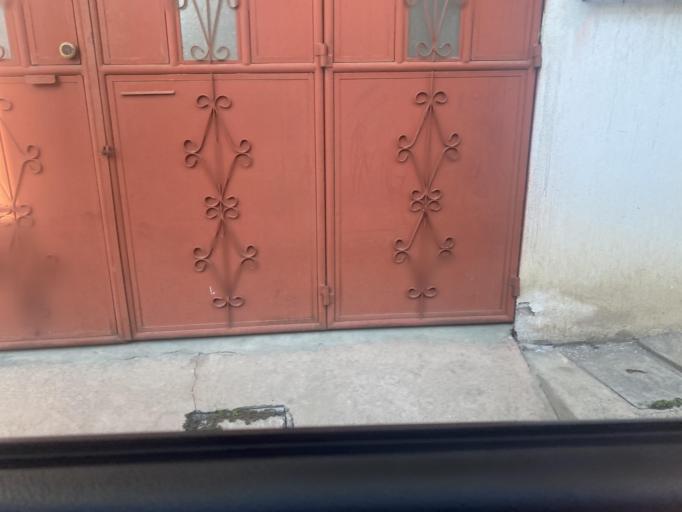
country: GT
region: Quetzaltenango
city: Olintepeque
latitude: 14.8684
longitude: -91.5170
